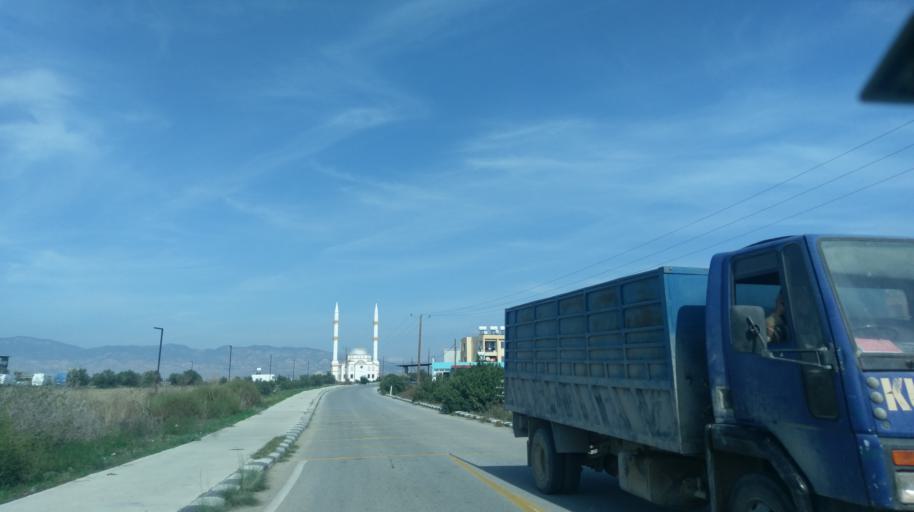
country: CY
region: Ammochostos
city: Lefkonoiko
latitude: 35.1875
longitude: 33.6397
